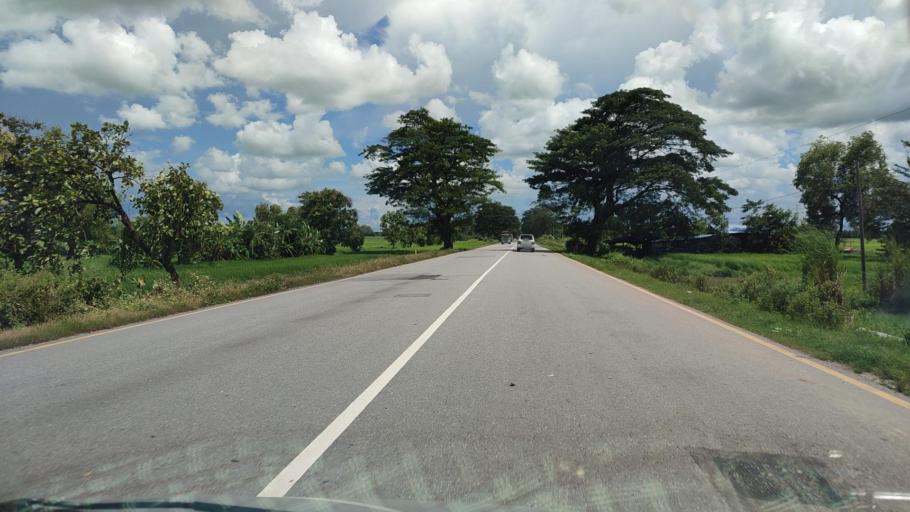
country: MM
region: Bago
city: Nyaunglebin
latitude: 18.0889
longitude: 96.6448
